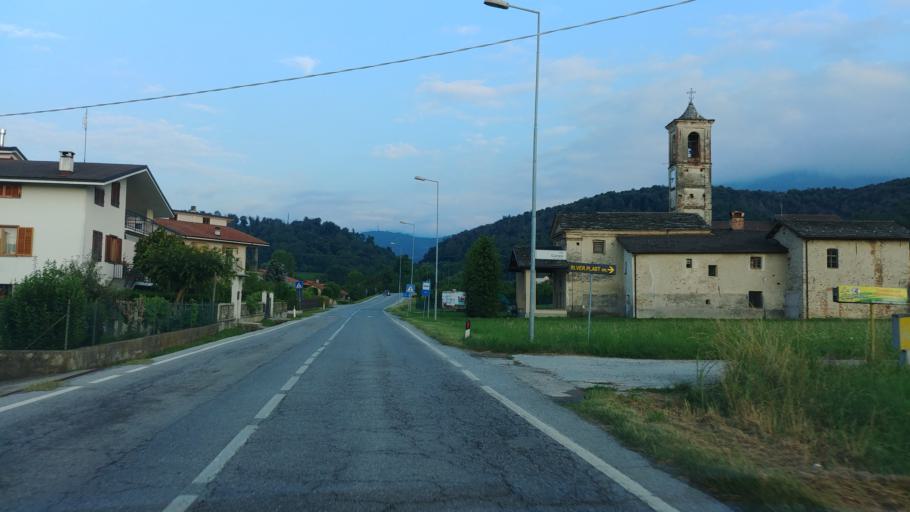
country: IT
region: Piedmont
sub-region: Provincia di Cuneo
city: Peveragno
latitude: 44.3380
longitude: 7.6030
